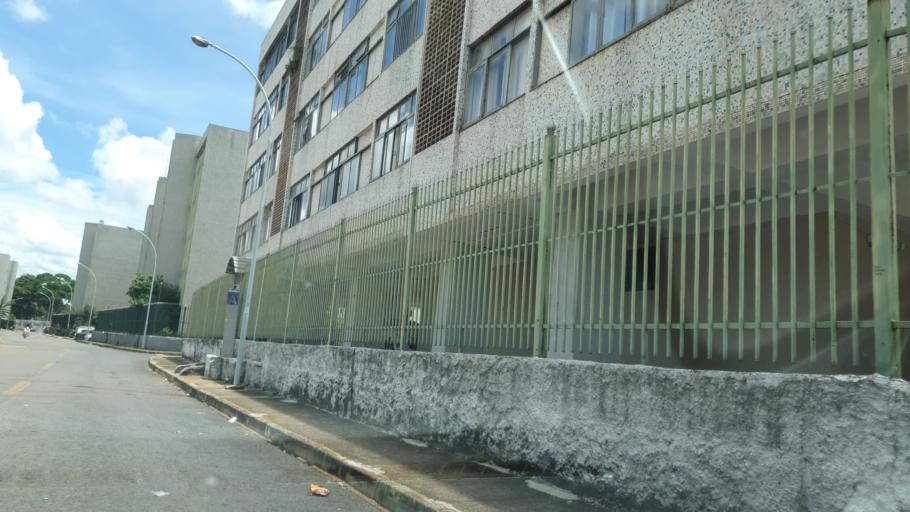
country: BR
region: Federal District
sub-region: Brasilia
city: Brasilia
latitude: -15.7959
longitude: -47.9424
